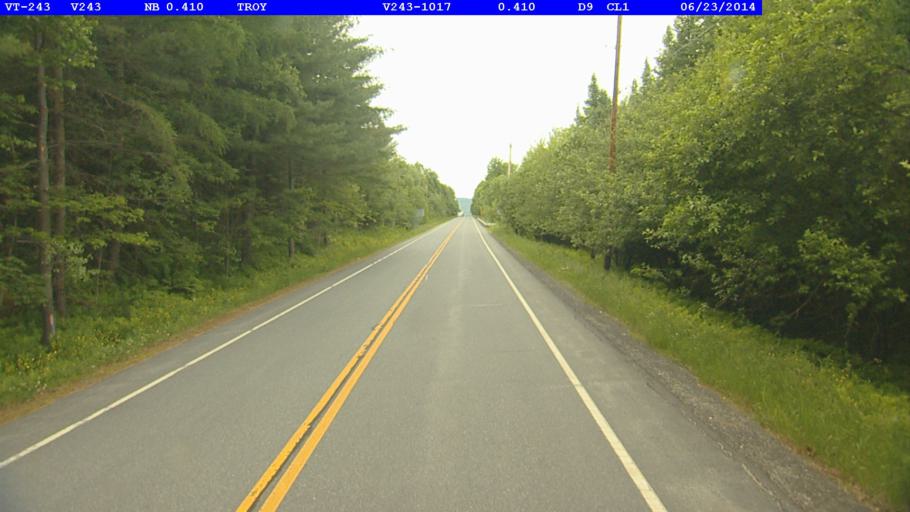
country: US
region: Vermont
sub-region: Orleans County
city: Newport
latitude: 45.0017
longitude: -72.4126
